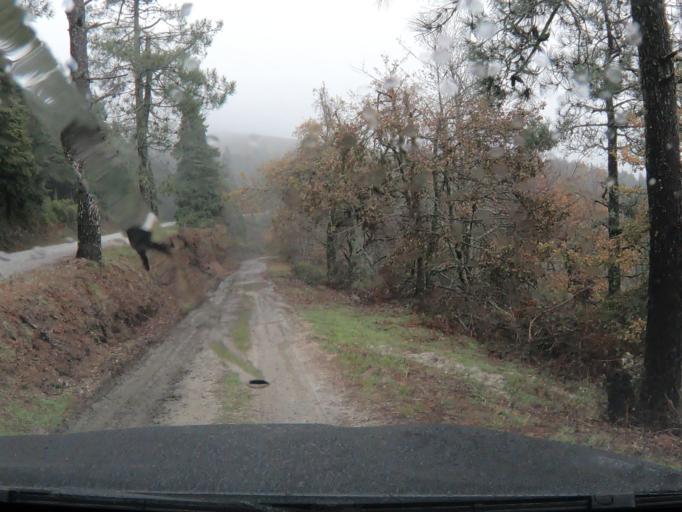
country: PT
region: Vila Real
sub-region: Mondim de Basto
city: Mondim de Basto
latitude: 41.3199
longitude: -7.8766
